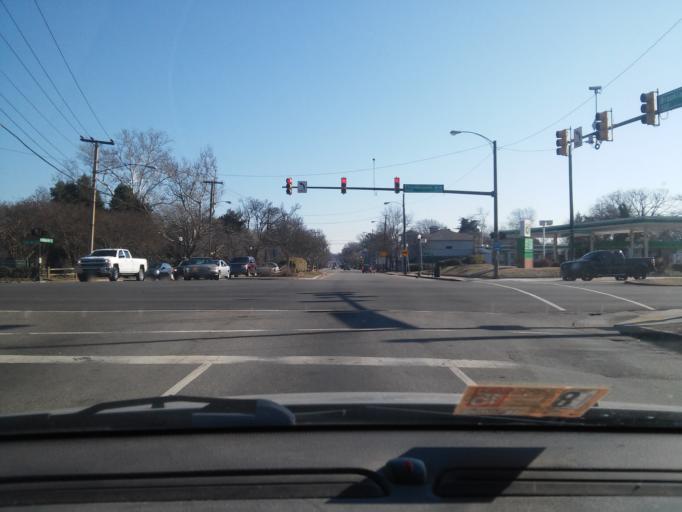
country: US
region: Virginia
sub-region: City of Richmond
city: Richmond
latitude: 37.5721
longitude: -77.4455
